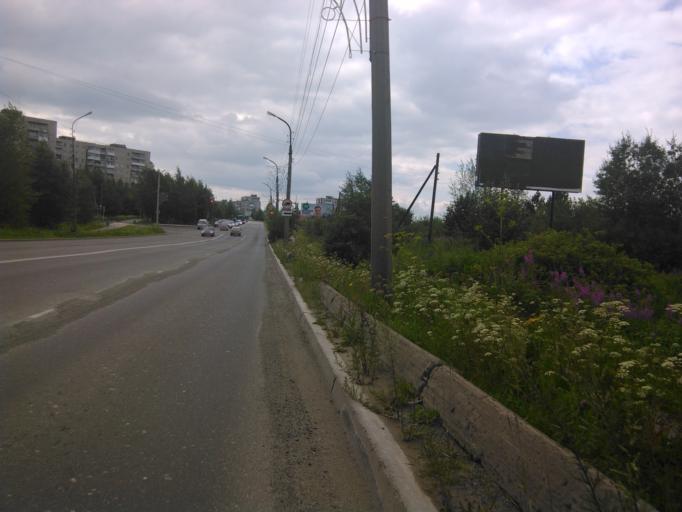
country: RU
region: Sverdlovsk
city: Krasnotur'insk
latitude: 59.7594
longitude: 60.1755
